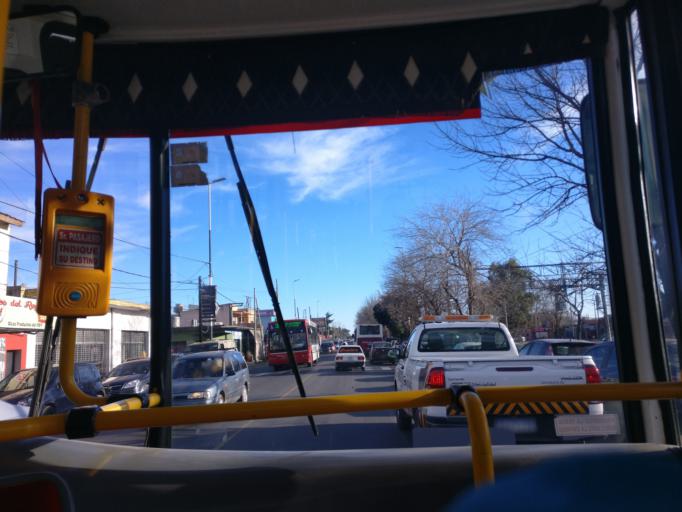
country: AR
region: Buenos Aires
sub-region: Partido de Ezeiza
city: Ezeiza
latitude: -34.8565
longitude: -58.5255
